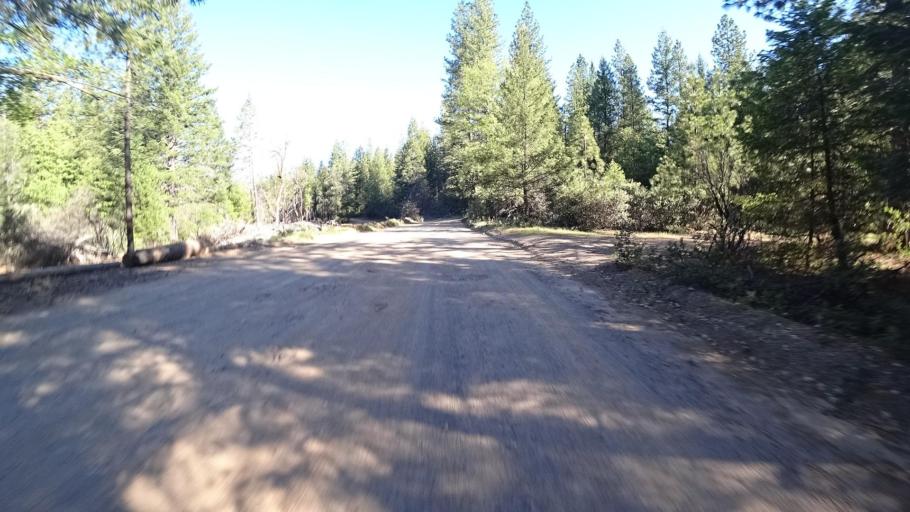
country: US
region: California
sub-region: Lake County
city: Upper Lake
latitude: 39.3532
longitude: -122.9775
